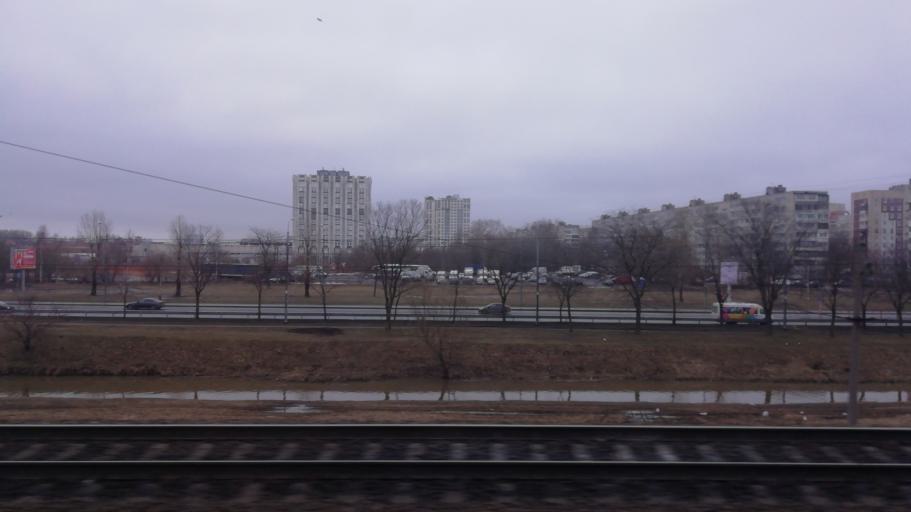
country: RU
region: St.-Petersburg
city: Kupchino
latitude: 59.8724
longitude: 30.3553
